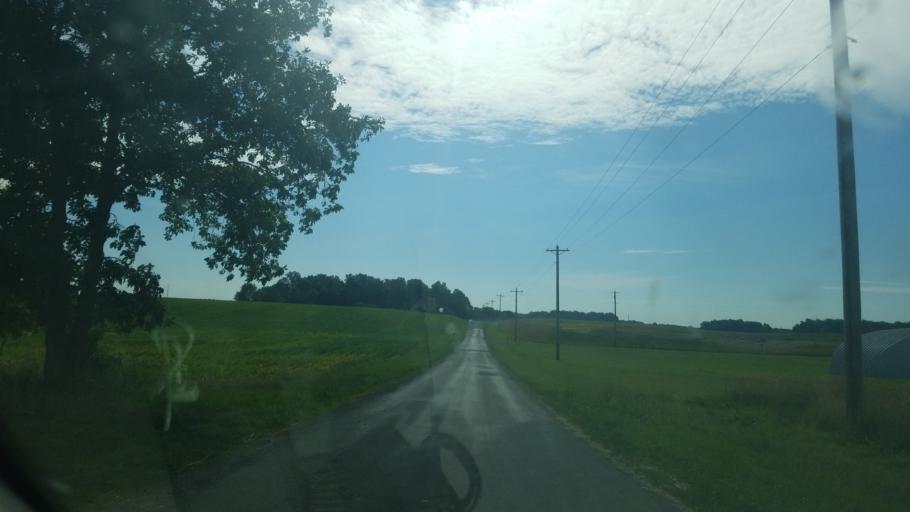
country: US
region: Ohio
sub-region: Wyandot County
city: Upper Sandusky
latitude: 40.7892
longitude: -83.2126
